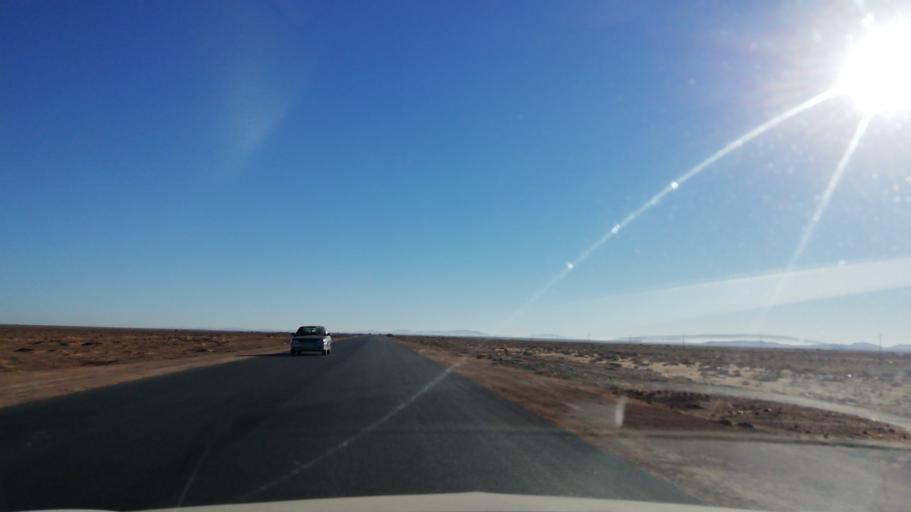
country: DZ
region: El Bayadh
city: El Bayadh
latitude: 33.8580
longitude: 0.5759
